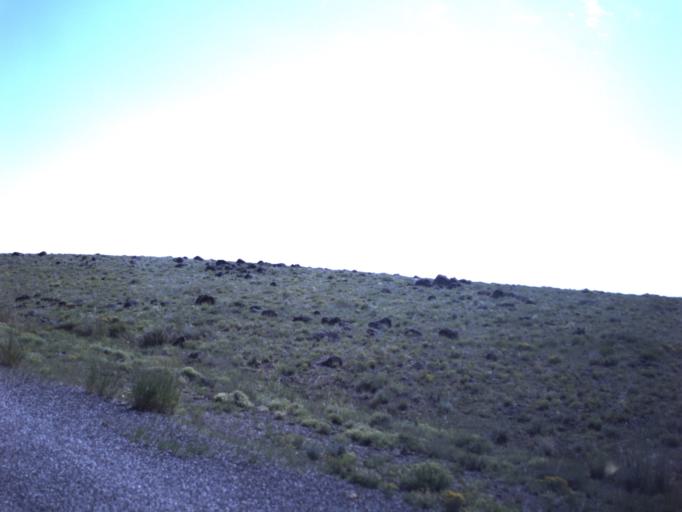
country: US
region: Utah
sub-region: Wayne County
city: Loa
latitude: 38.5822
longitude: -111.4787
